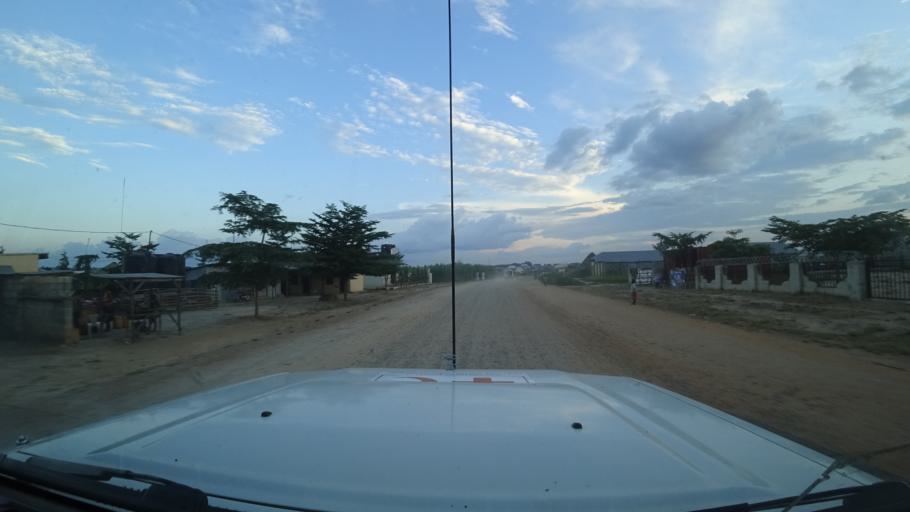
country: NG
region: Niger
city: Minna
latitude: 9.6470
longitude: 6.5811
